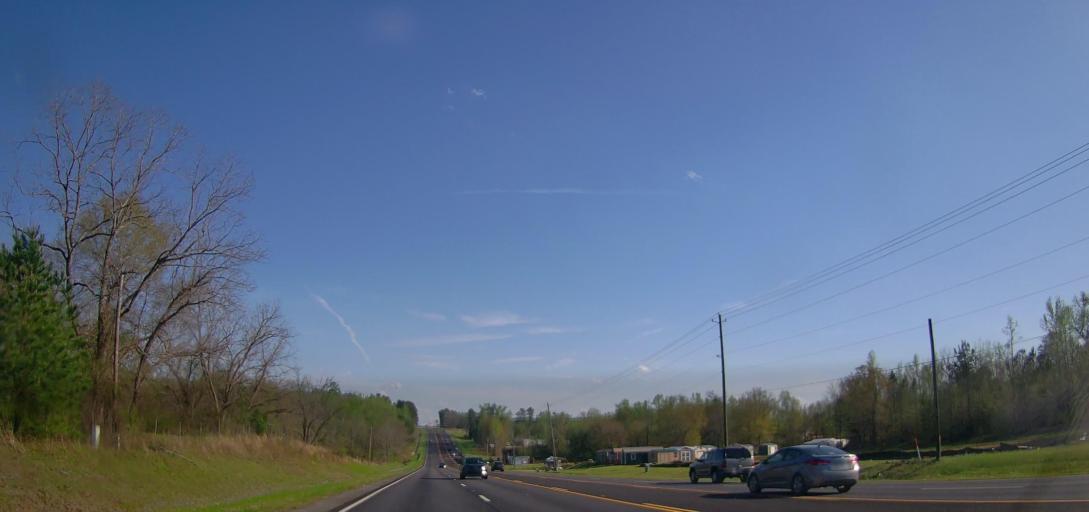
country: US
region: Georgia
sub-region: Baldwin County
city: Milledgeville
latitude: 33.1636
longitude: -83.2790
